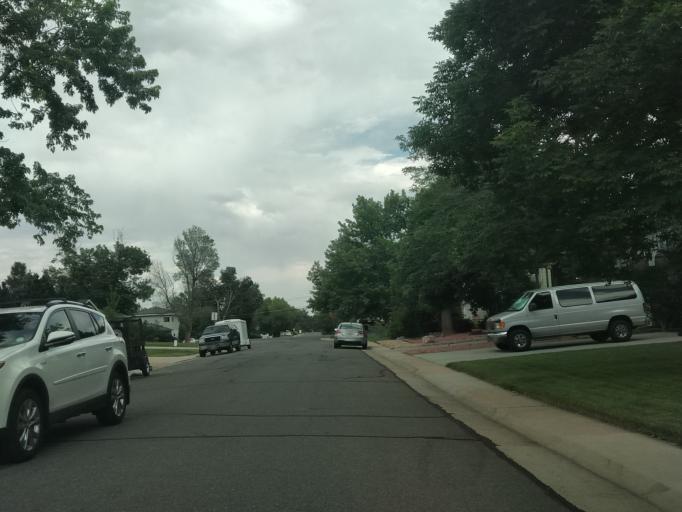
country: US
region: Colorado
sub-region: Jefferson County
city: Lakewood
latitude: 39.7001
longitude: -105.1014
